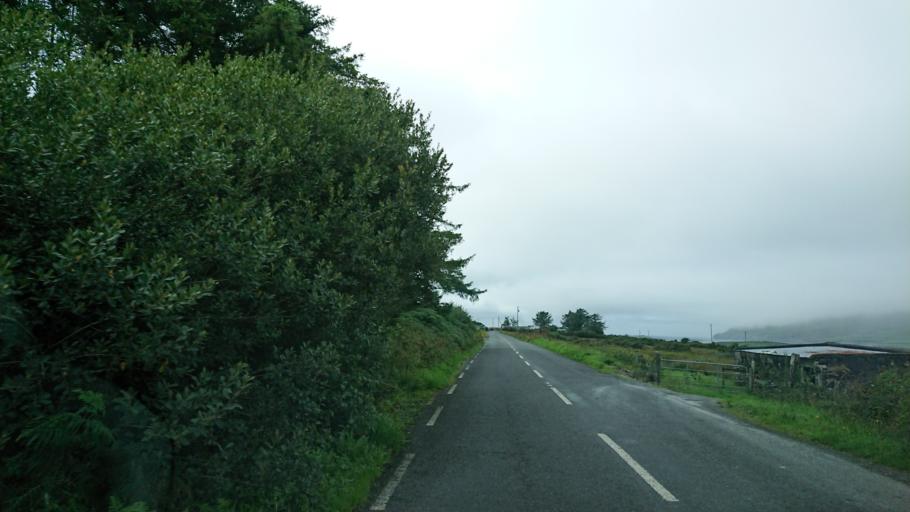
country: IE
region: Munster
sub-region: Ciarrai
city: Cahersiveen
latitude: 51.9326
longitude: -10.2526
